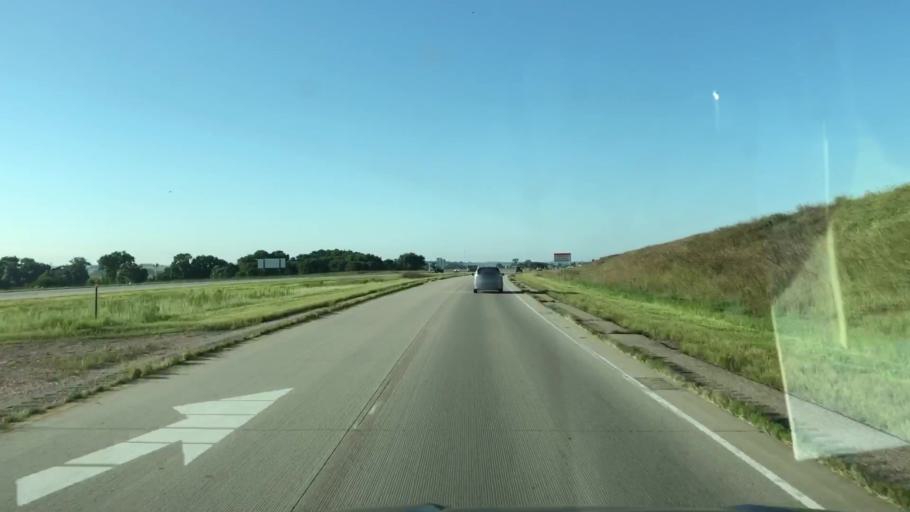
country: US
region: Iowa
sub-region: Plymouth County
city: Le Mars
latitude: 42.7562
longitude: -96.2096
